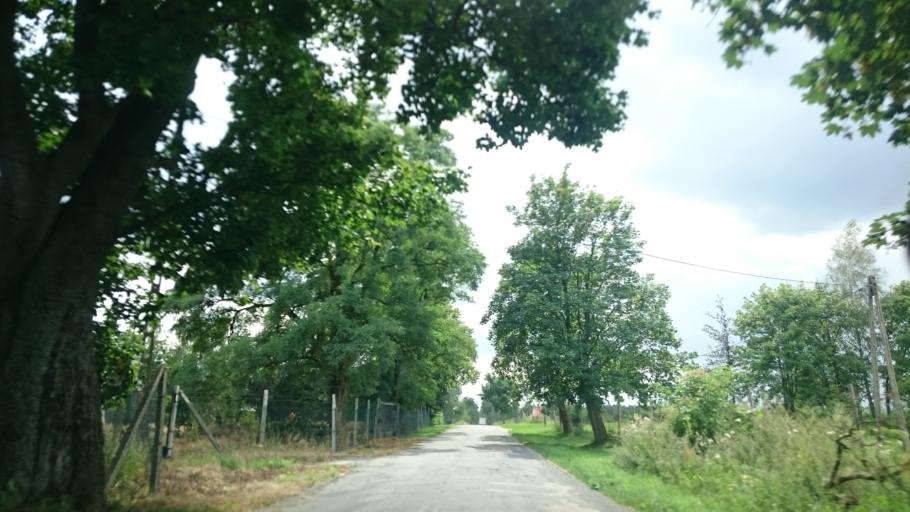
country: PL
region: Pomeranian Voivodeship
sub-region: Powiat chojnicki
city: Chojnice
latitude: 53.6800
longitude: 17.6760
